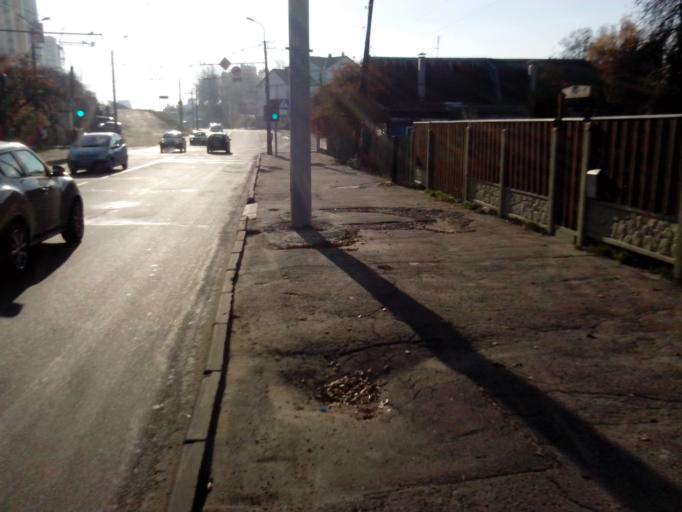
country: BY
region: Minsk
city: Minsk
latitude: 53.9414
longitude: 27.5863
